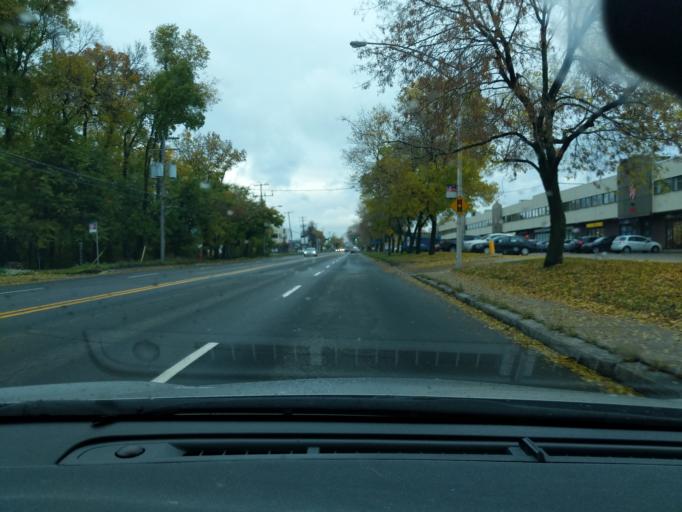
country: CA
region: Quebec
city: L'Ancienne-Lorette
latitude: 46.8062
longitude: -71.3075
